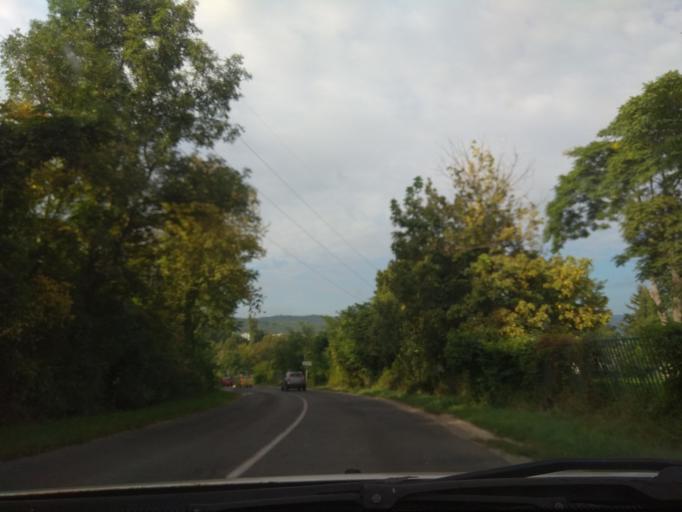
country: HU
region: Borsod-Abauj-Zemplen
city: Miskolc
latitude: 48.0883
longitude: 20.7313
